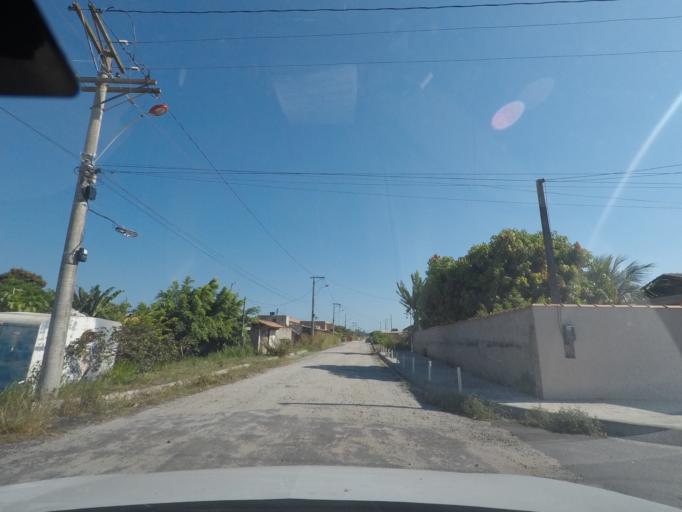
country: BR
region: Rio de Janeiro
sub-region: Marica
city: Marica
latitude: -22.9593
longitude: -42.9245
